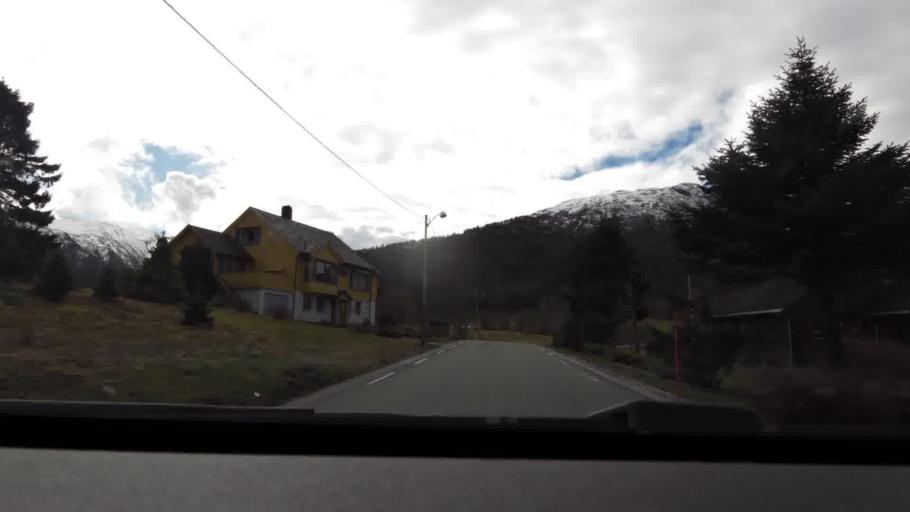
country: NO
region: More og Romsdal
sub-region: Eide
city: Eide
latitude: 62.9110
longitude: 7.5405
